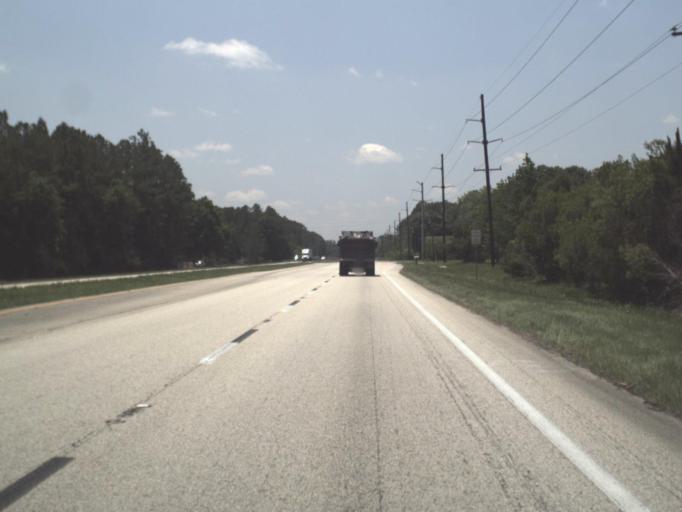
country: US
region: Florida
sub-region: Bradford County
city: Starke
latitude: 30.0832
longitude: -82.0629
